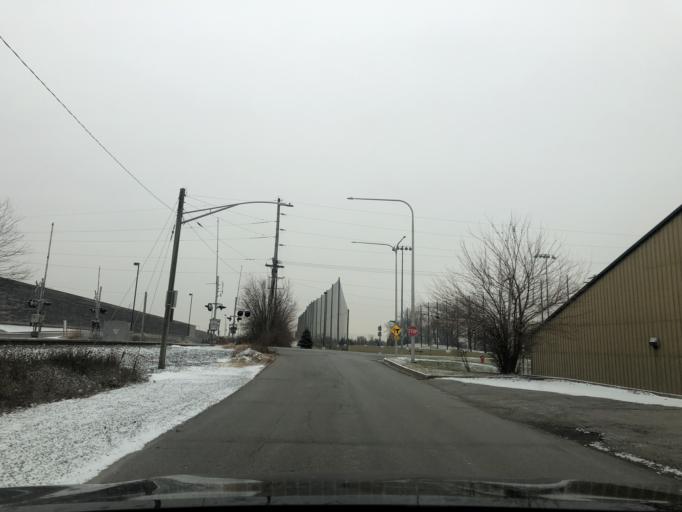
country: US
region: Illinois
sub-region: Cook County
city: Evergreen Park
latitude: 41.7287
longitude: -87.6874
